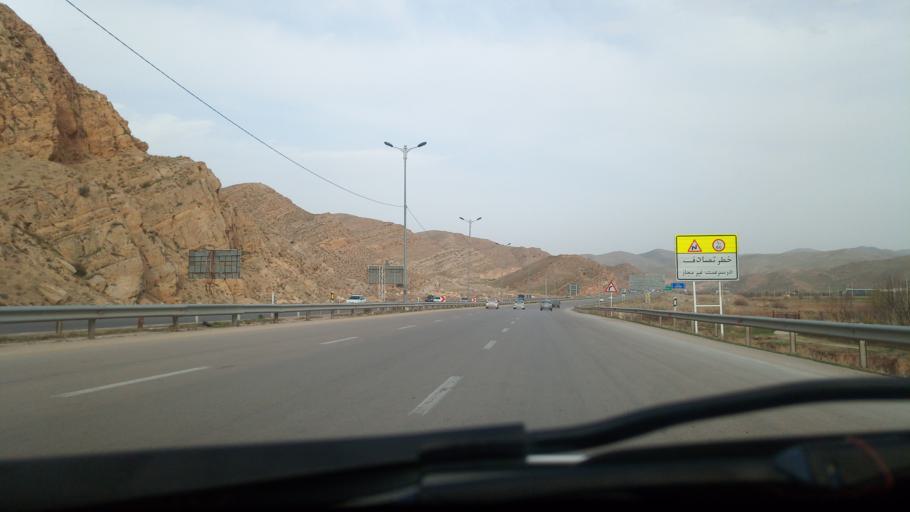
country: IR
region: Khorasan-e Shomali
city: Bojnurd
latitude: 37.4804
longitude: 57.4069
